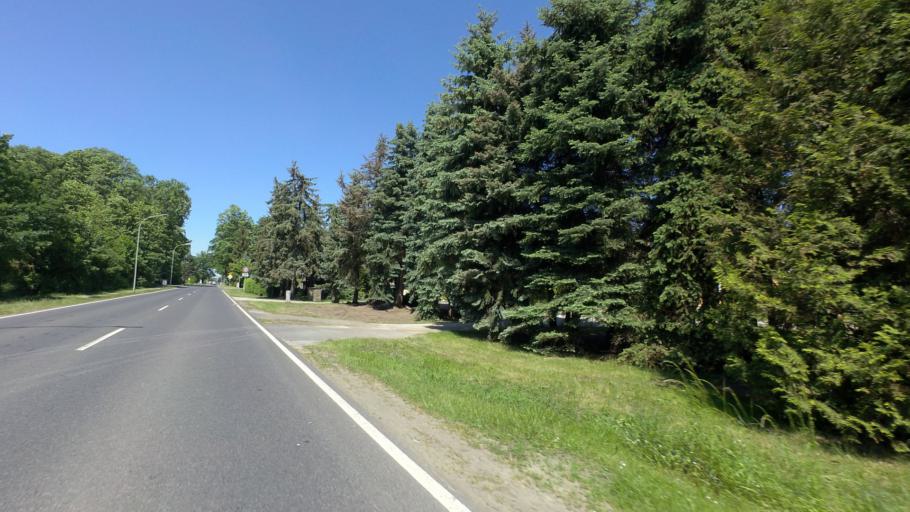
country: DE
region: Brandenburg
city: Drehnow
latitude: 51.8723
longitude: 14.3783
